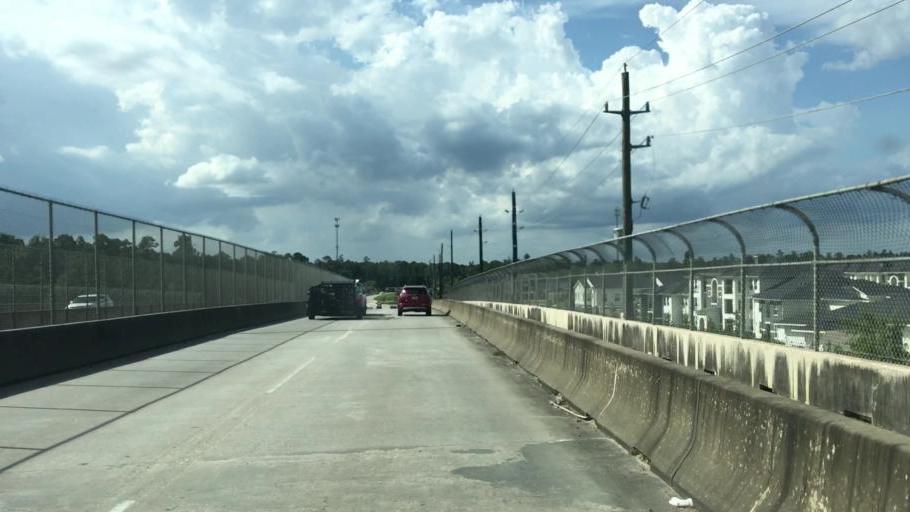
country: US
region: Texas
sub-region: Harris County
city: Atascocita
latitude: 29.9676
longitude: -95.1699
